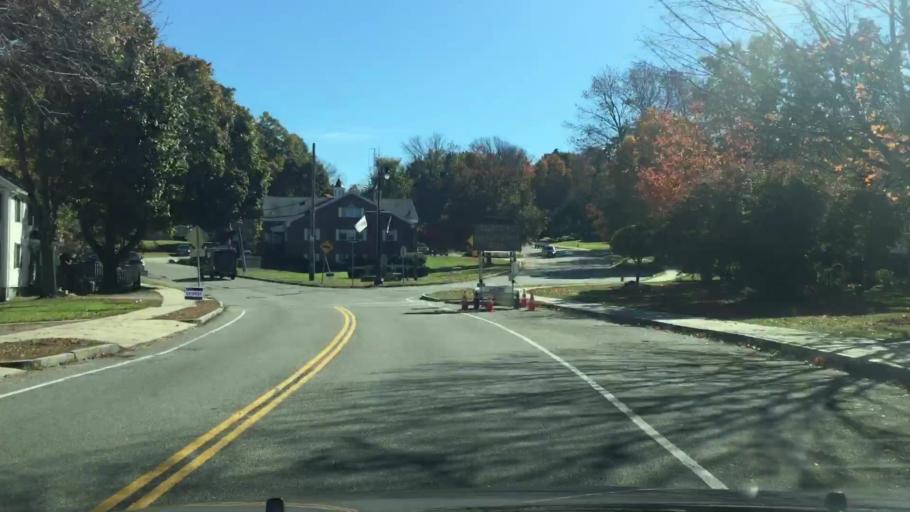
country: US
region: Massachusetts
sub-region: Essex County
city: North Andover
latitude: 42.6840
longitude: -71.1129
